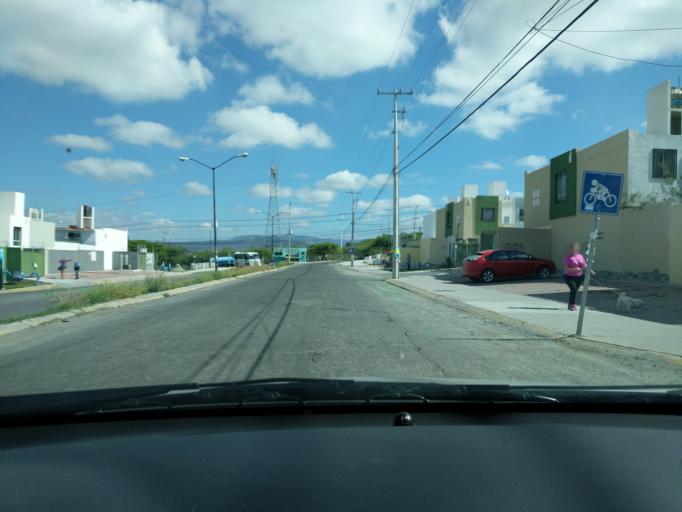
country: MX
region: Queretaro
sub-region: Queretaro
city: Patria Nueva
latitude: 20.6448
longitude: -100.4812
